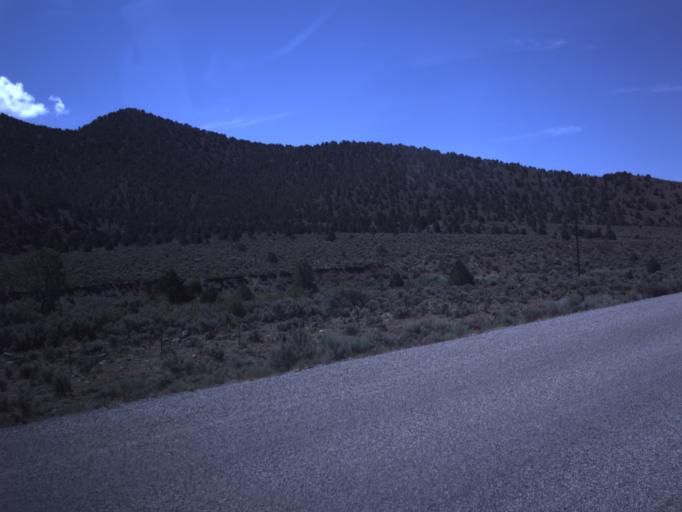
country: US
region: Utah
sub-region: Piute County
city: Junction
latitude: 38.0712
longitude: -112.3426
